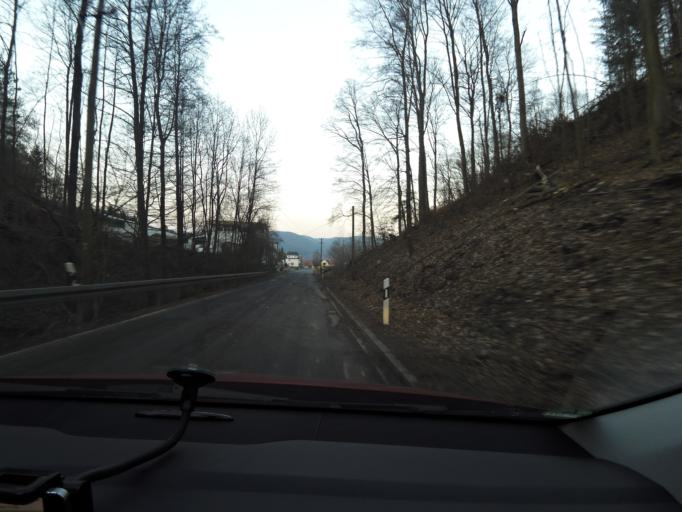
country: DE
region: Hesse
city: Witzenhausen
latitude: 51.3522
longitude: 9.8098
